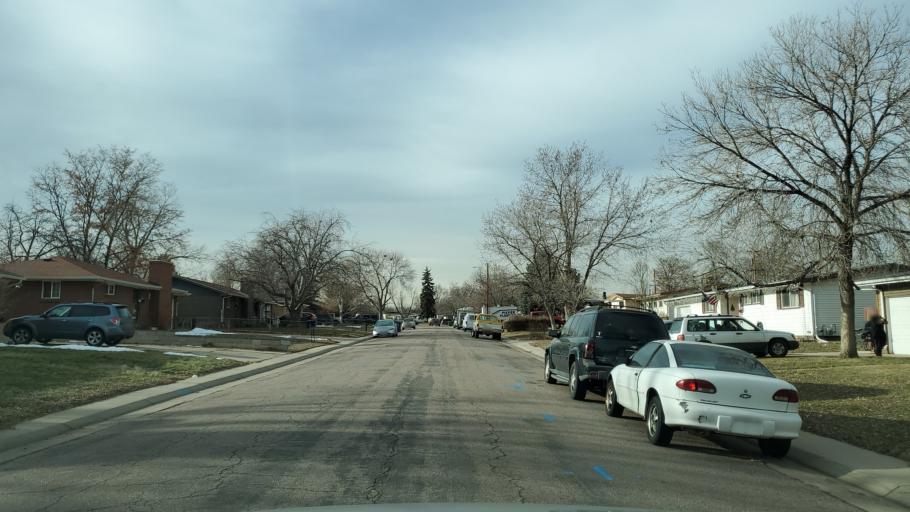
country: US
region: Colorado
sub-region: Adams County
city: Sherrelwood
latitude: 39.8364
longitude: -105.0176
